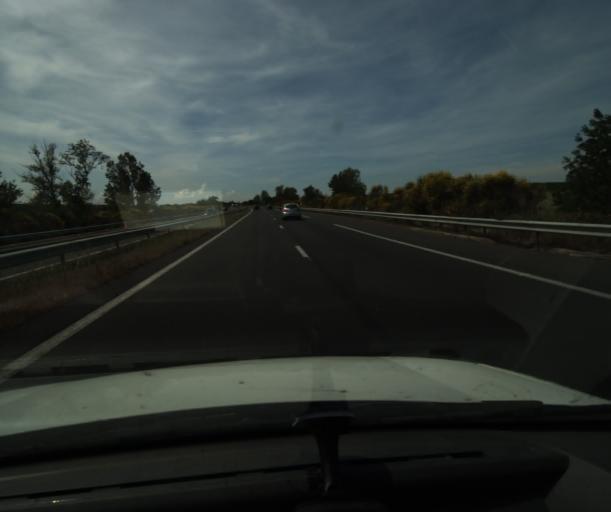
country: FR
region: Languedoc-Roussillon
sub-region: Departement de l'Aude
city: Villeneuve-la-Comptal
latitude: 43.3057
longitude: 1.9140
